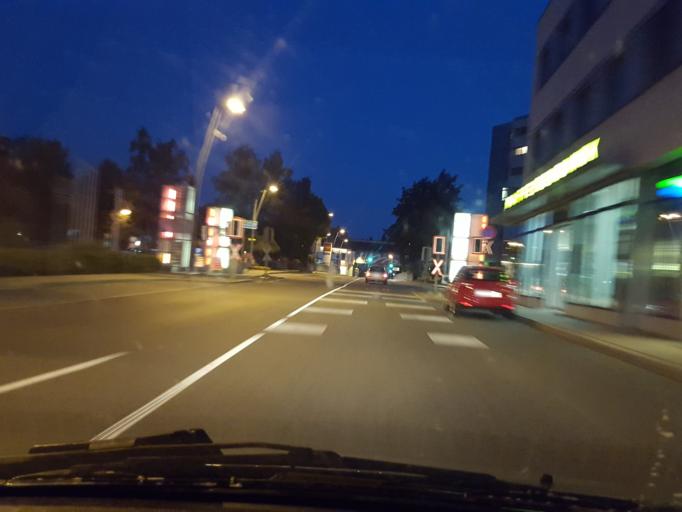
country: AT
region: Lower Austria
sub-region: Politischer Bezirk Scheibbs
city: Wieselburg
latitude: 48.1302
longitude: 15.1386
